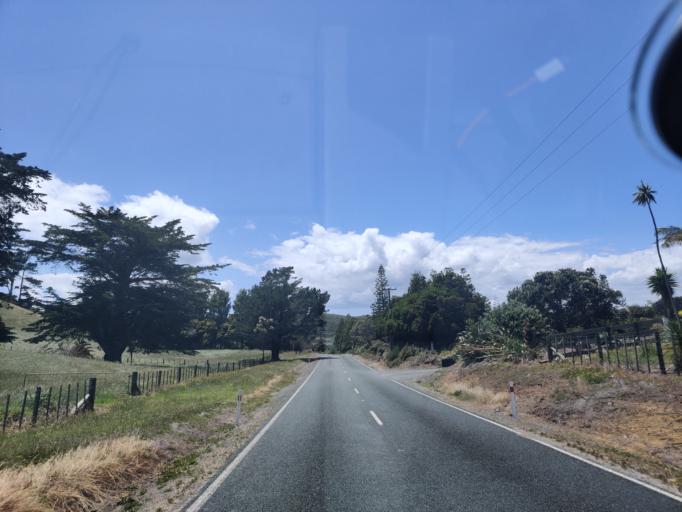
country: NZ
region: Northland
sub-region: Far North District
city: Kaitaia
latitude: -35.0286
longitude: 173.1916
